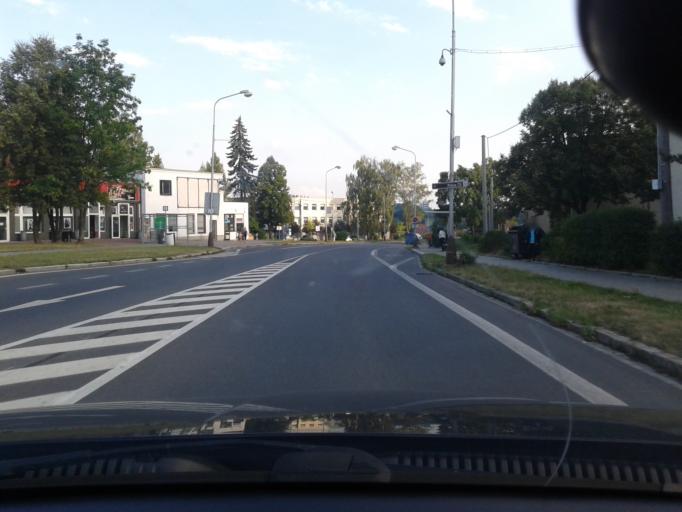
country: CZ
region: Moravskoslezsky
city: Orlova
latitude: 49.8607
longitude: 18.4249
